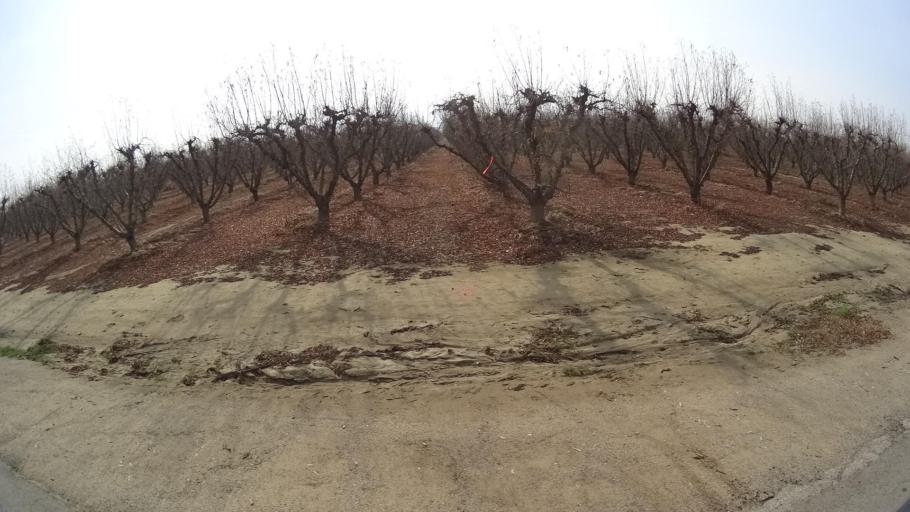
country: US
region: California
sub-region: Kern County
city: Greenfield
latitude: 35.0764
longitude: -119.0227
